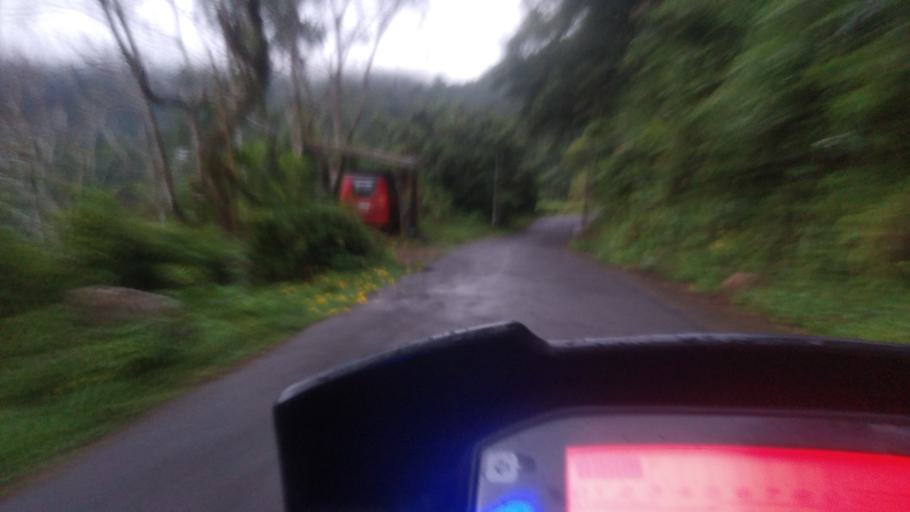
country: IN
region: Kerala
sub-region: Kottayam
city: Erattupetta
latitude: 9.5533
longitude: 76.9717
